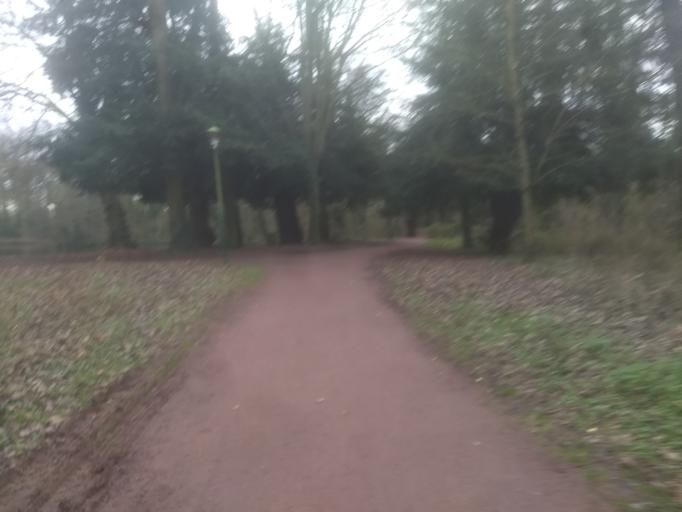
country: FR
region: Nord-Pas-de-Calais
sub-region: Departement du Pas-de-Calais
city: Saint-Laurent-Blangy
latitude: 50.3017
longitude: 2.8106
